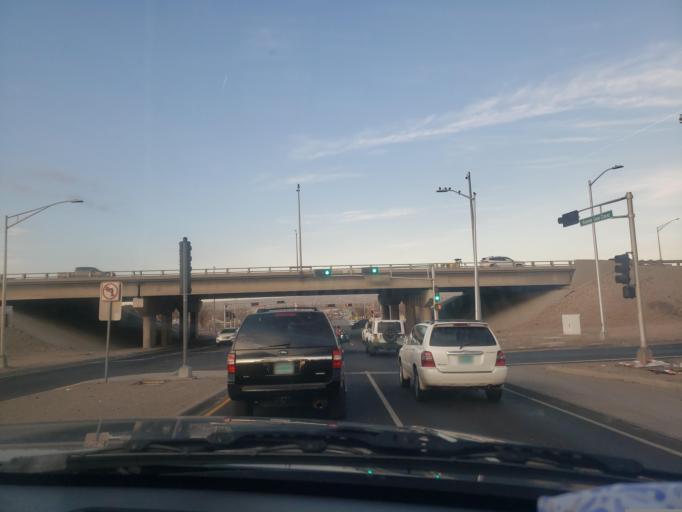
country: US
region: New Mexico
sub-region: Bernalillo County
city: Albuquerque
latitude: 35.0699
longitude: -106.6388
